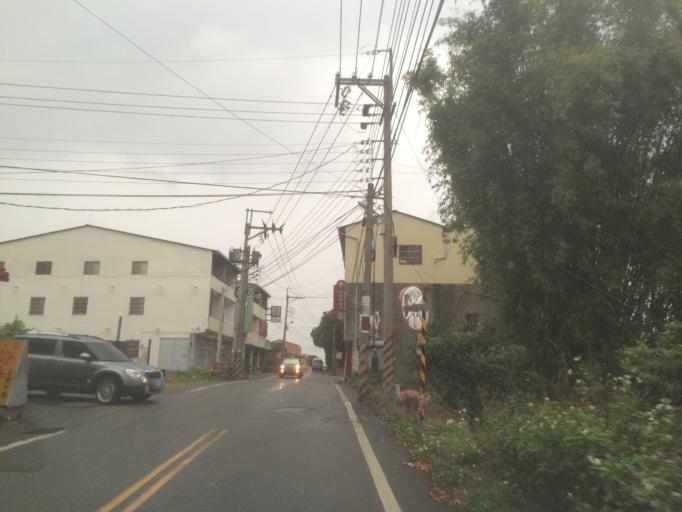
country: TW
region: Taiwan
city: Fengyuan
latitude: 24.1955
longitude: 120.8050
